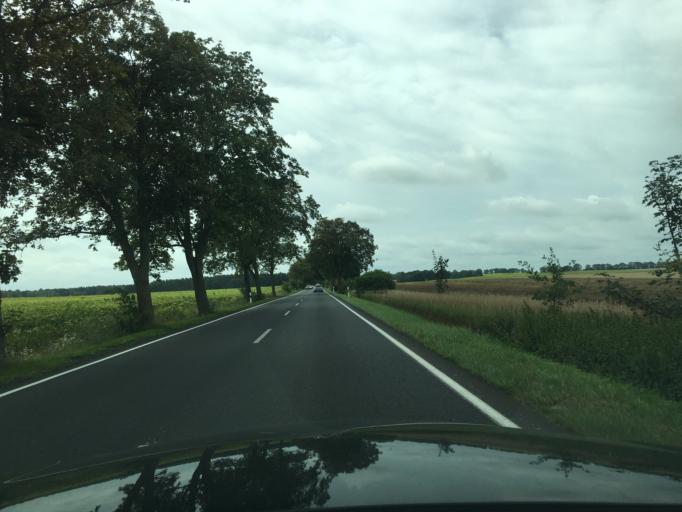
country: DE
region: Brandenburg
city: Gransee
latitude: 52.9308
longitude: 13.1551
